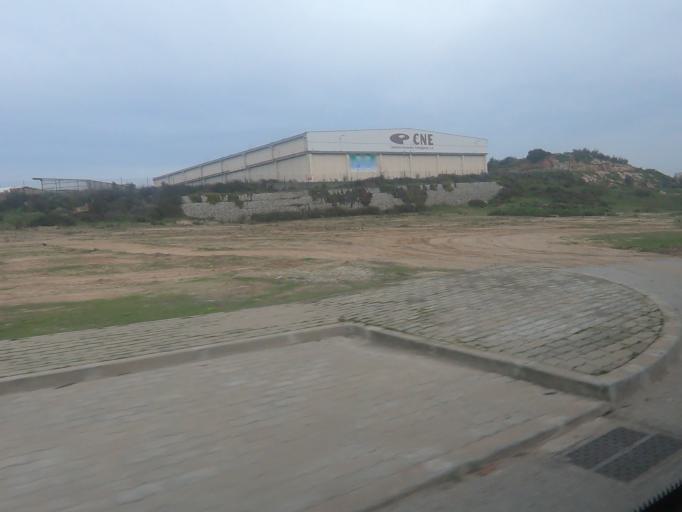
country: PT
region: Setubal
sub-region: Setubal
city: Setubal
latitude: 38.4945
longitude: -8.8279
